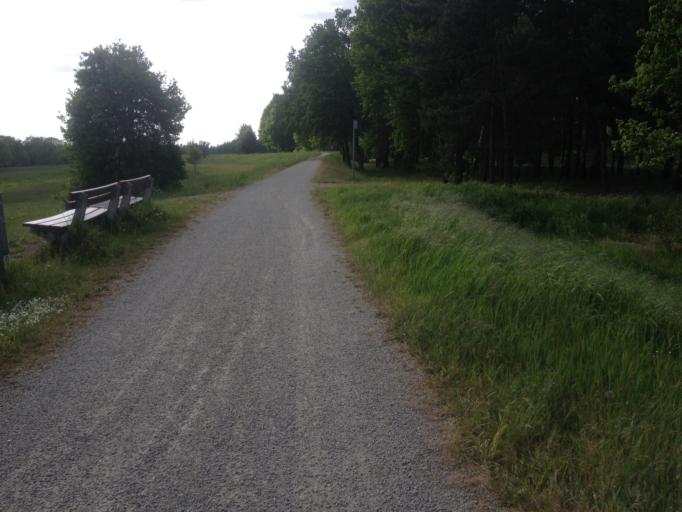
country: DE
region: Brandenburg
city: Drehnow
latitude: 51.8499
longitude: 14.3212
